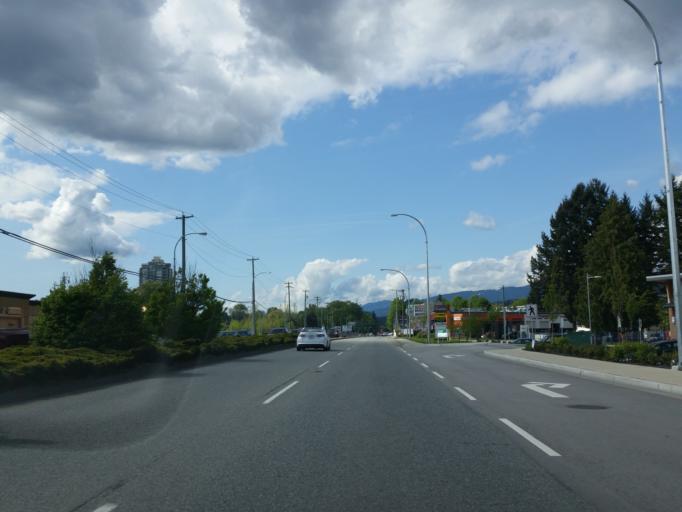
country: CA
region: British Columbia
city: Coquitlam
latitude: 49.2643
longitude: -122.7686
